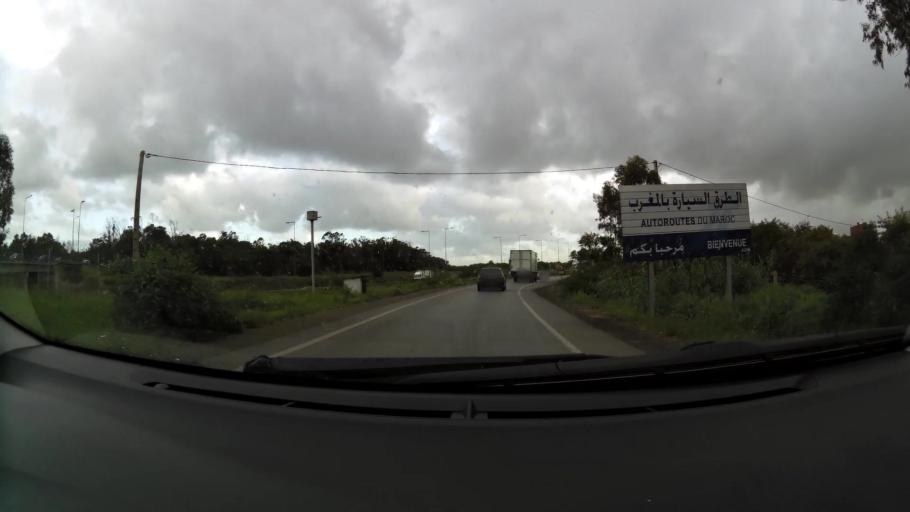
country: MA
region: Grand Casablanca
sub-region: Mohammedia
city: Mohammedia
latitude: 33.6625
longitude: -7.4046
